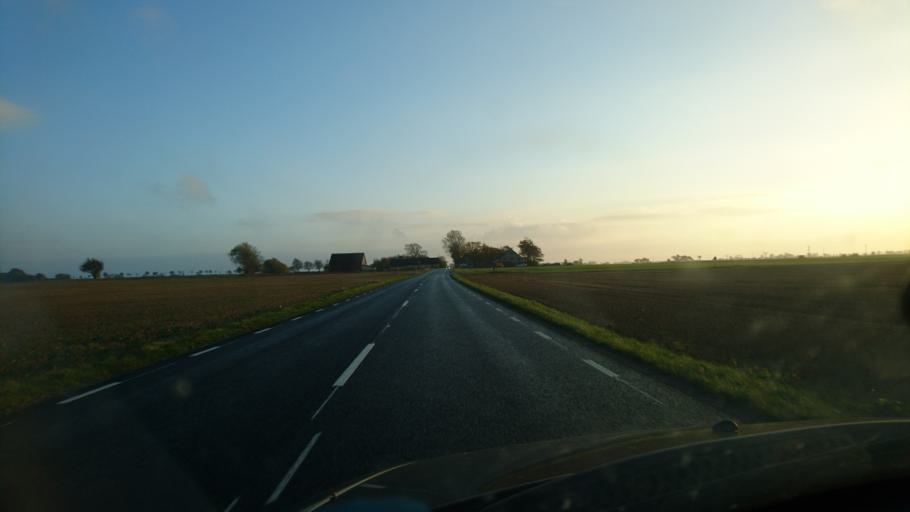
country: SE
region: Skane
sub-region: Simrishamns Kommun
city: Simrishamn
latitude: 55.4459
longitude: 14.1765
